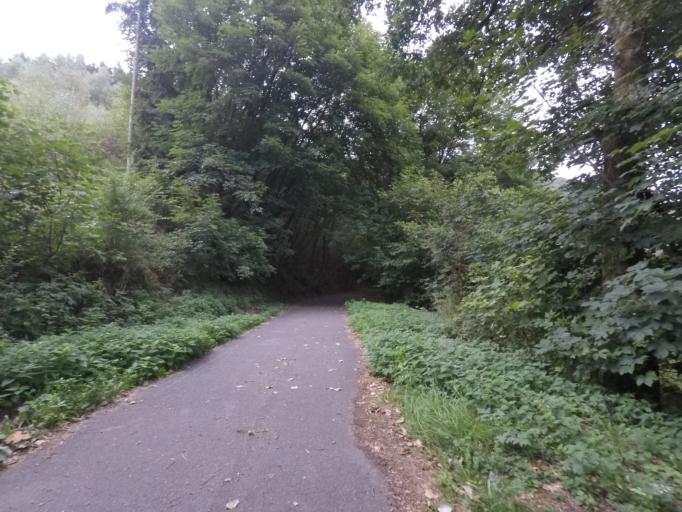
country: BE
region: Wallonia
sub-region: Province du Luxembourg
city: Martelange
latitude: 49.8426
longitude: 5.7271
